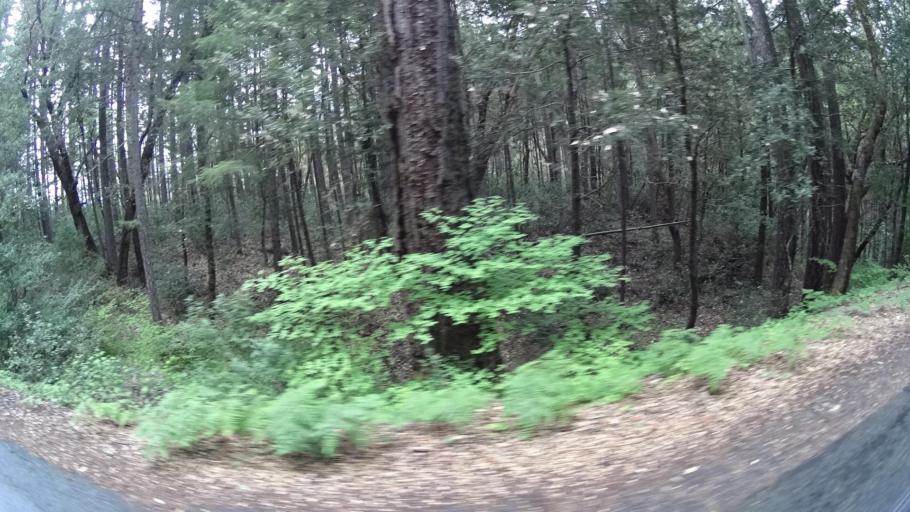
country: US
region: California
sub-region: Humboldt County
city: Willow Creek
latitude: 41.3495
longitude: -123.5120
